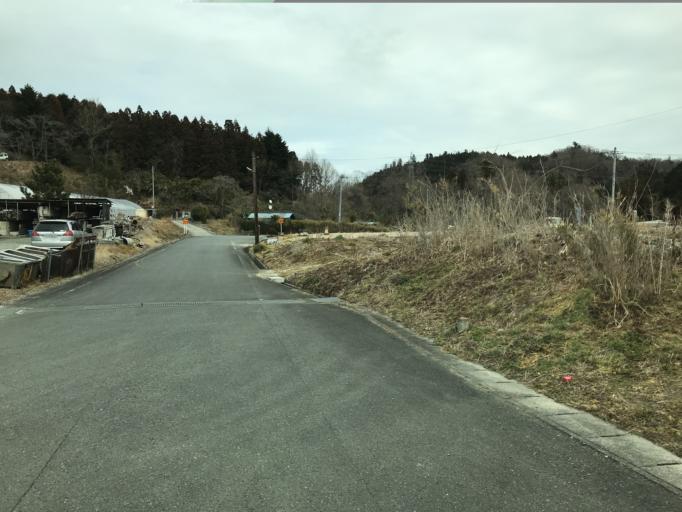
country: JP
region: Fukushima
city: Iwaki
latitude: 37.1035
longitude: 140.8766
